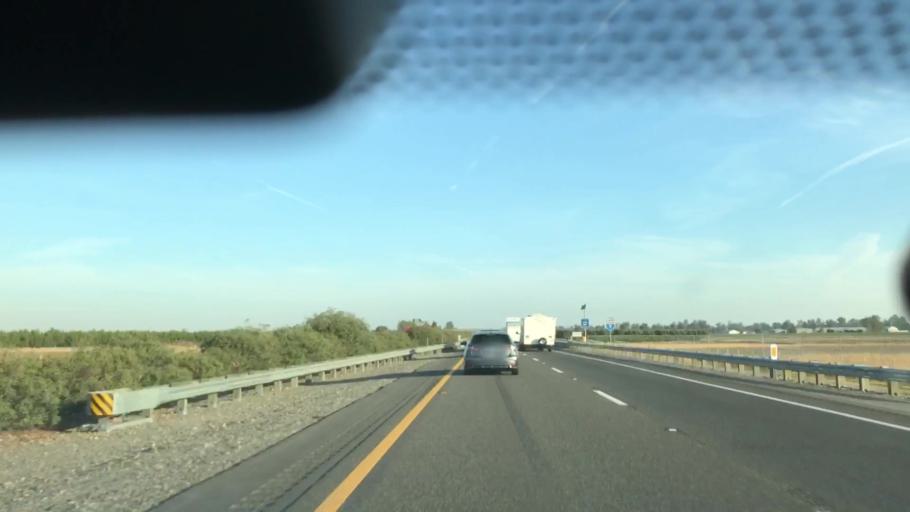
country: US
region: California
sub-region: Glenn County
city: Orland
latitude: 39.6892
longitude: -122.2048
